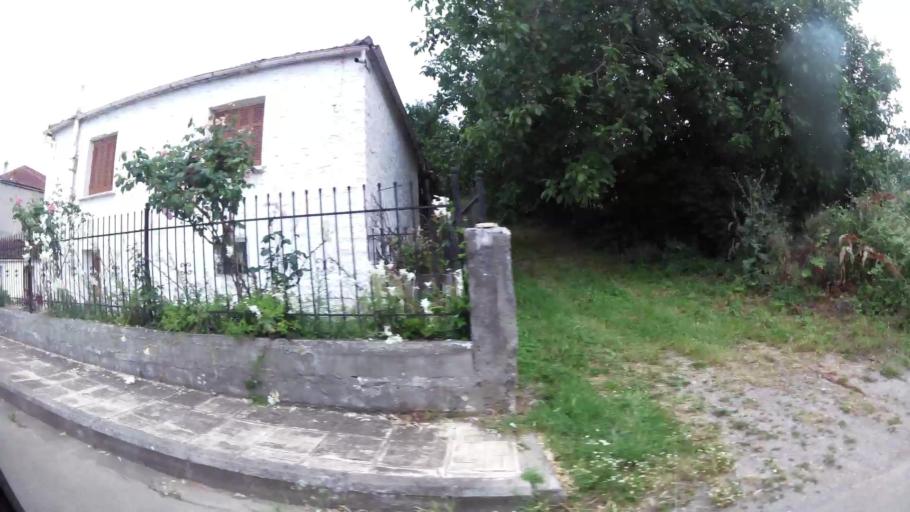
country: GR
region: West Macedonia
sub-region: Nomos Kozanis
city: Koila
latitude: 40.3488
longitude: 21.8358
